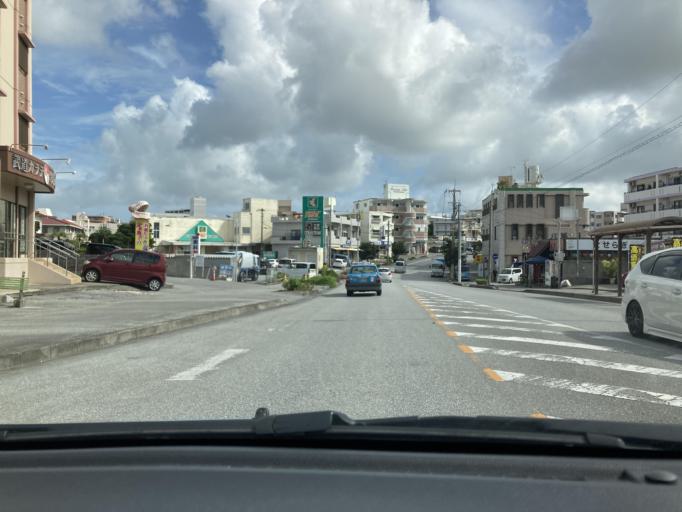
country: JP
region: Okinawa
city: Tomigusuku
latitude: 26.1697
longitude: 127.6930
